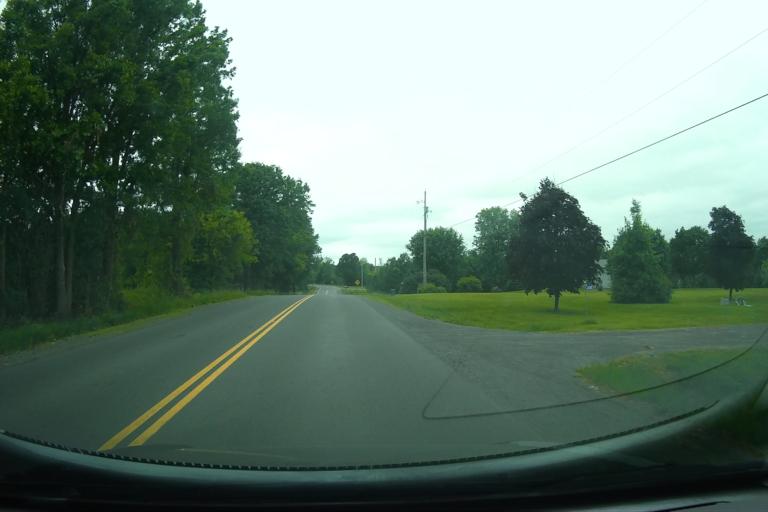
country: CA
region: Ontario
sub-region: Lanark County
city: Smiths Falls
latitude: 44.9807
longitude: -75.7900
